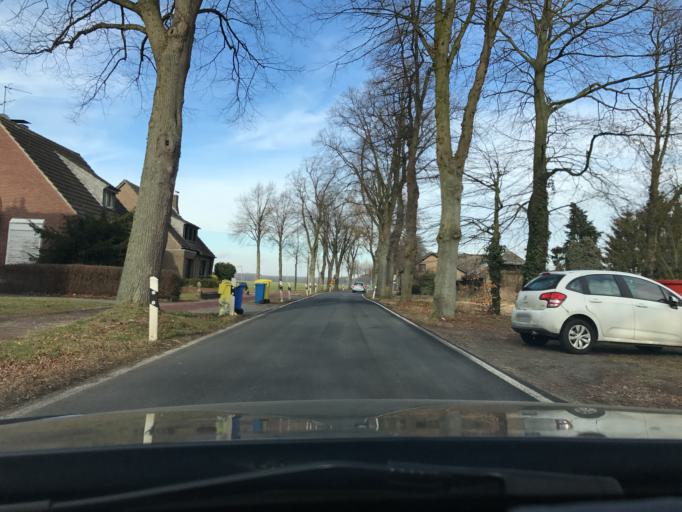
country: DE
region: North Rhine-Westphalia
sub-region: Regierungsbezirk Dusseldorf
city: Grefrath
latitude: 51.3488
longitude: 6.3642
